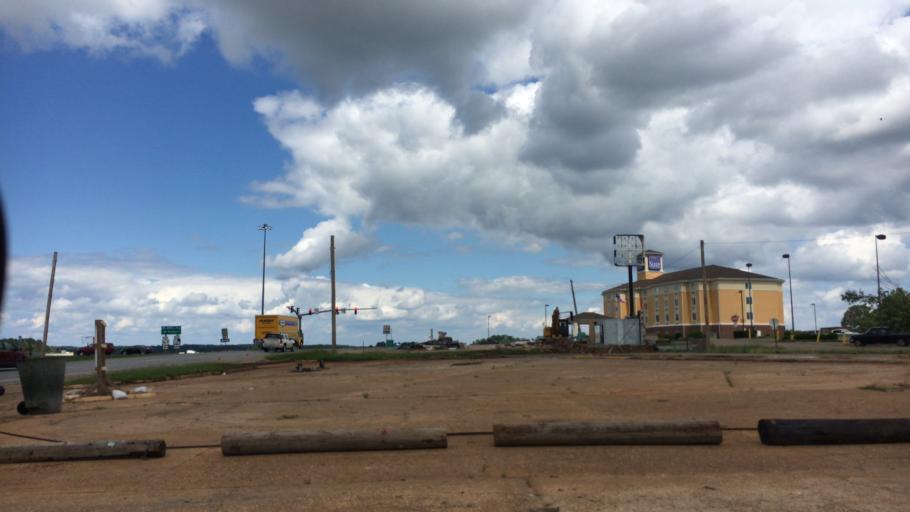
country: US
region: Louisiana
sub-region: Lincoln Parish
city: Ruston
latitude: 32.5392
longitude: -92.6391
